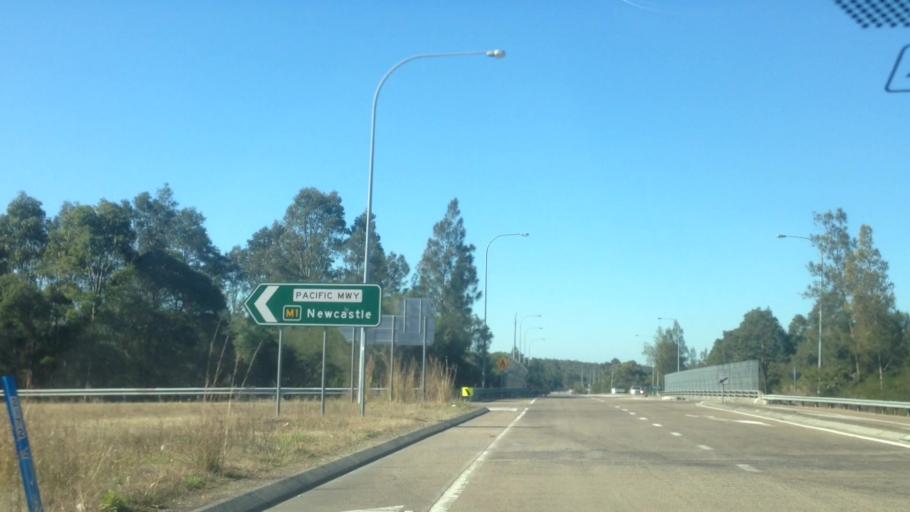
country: AU
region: New South Wales
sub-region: Lake Macquarie Shire
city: Cooranbong
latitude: -33.1191
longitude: 151.4645
